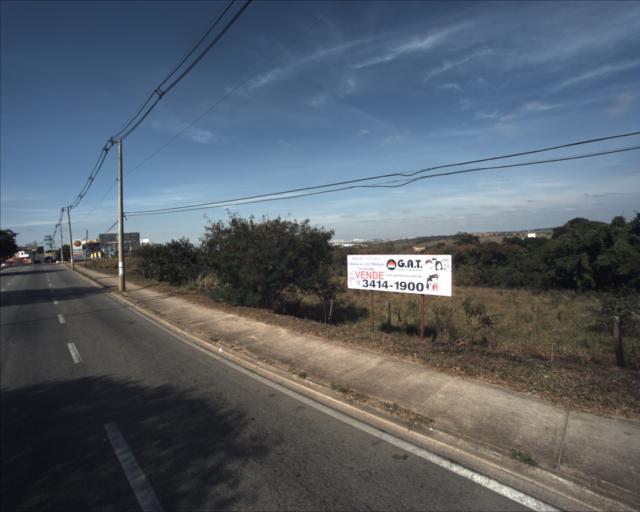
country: BR
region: Sao Paulo
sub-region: Sorocaba
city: Sorocaba
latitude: -23.4515
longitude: -47.5123
